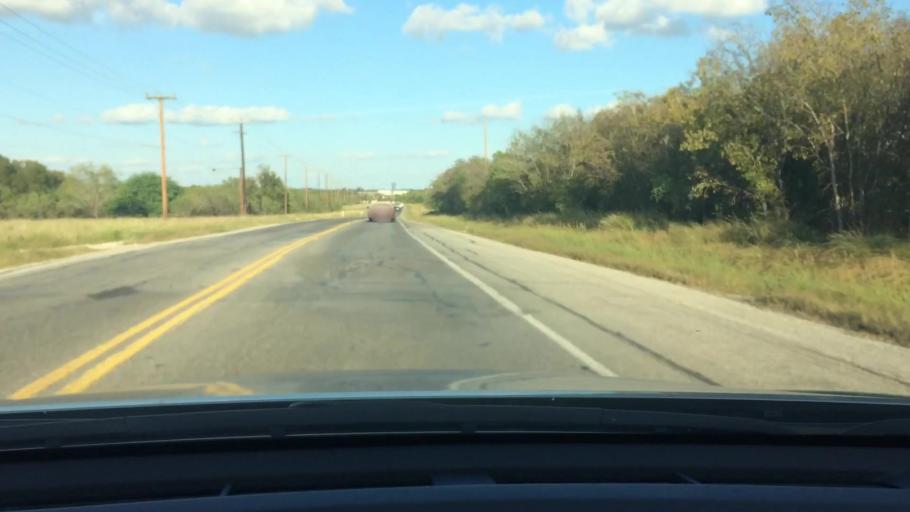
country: US
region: Texas
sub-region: Bexar County
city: Converse
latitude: 29.5109
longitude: -98.3335
